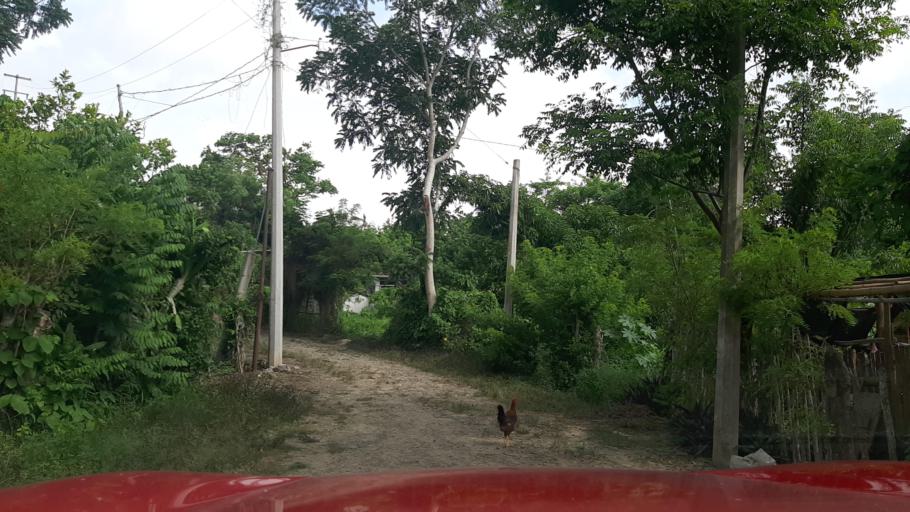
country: MX
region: Veracruz
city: Cazones de Herrera
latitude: 20.6754
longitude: -97.3255
